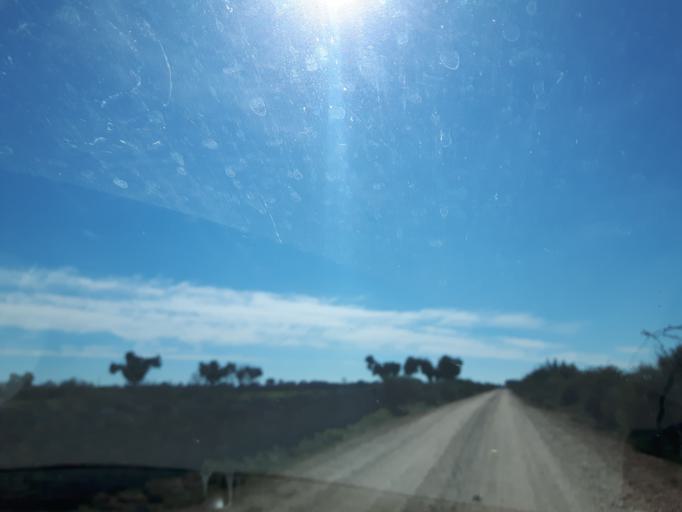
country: ES
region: Castille and Leon
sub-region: Provincia de Salamanca
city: Bermellar
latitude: 40.9623
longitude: -6.6668
